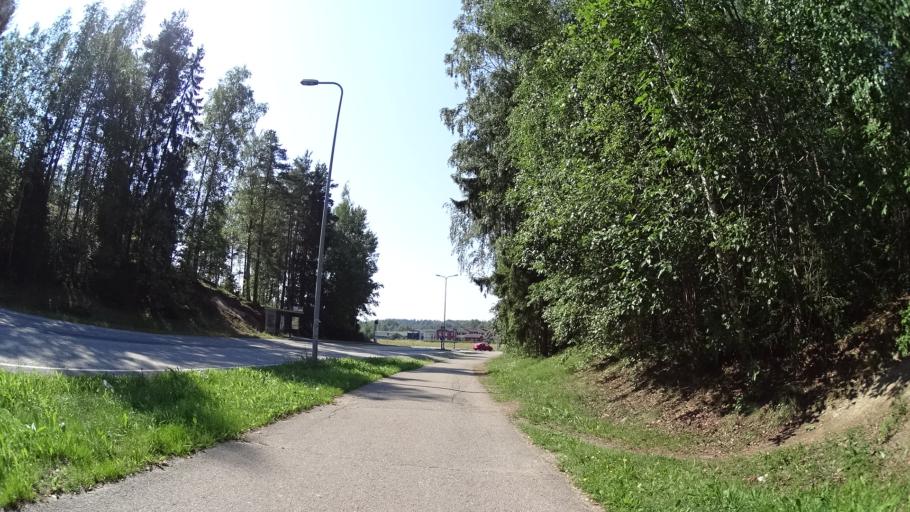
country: FI
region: Uusimaa
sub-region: Helsinki
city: Kerava
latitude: 60.3690
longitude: 25.0753
